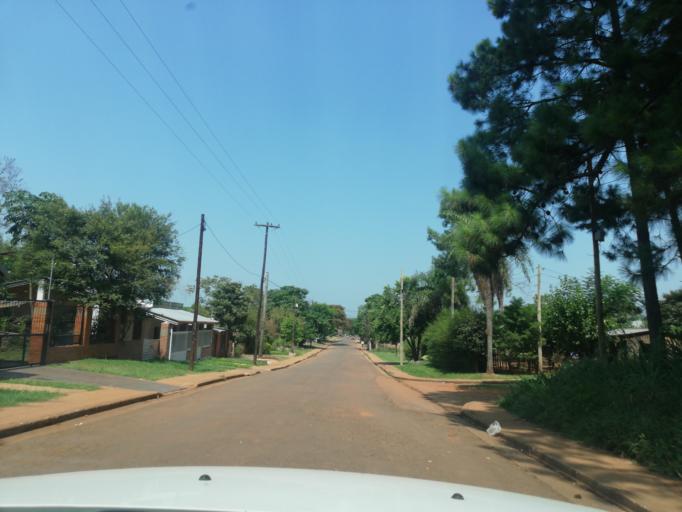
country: AR
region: Misiones
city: Garupa
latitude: -27.4414
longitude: -55.8858
